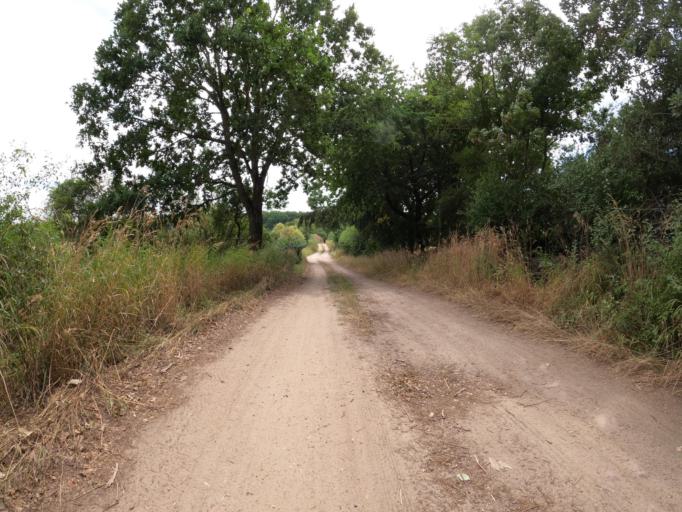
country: DE
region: Mecklenburg-Vorpommern
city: Loitz
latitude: 53.3904
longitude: 13.4449
